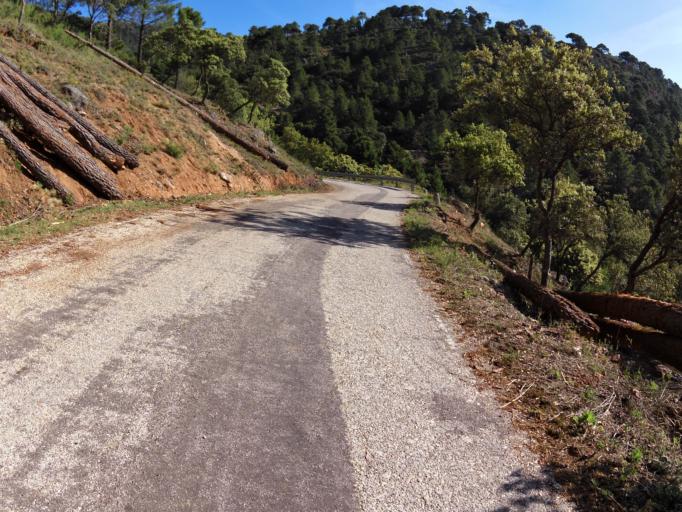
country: ES
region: Castille-La Mancha
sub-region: Provincia de Albacete
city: Riopar
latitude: 38.5227
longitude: -2.4559
